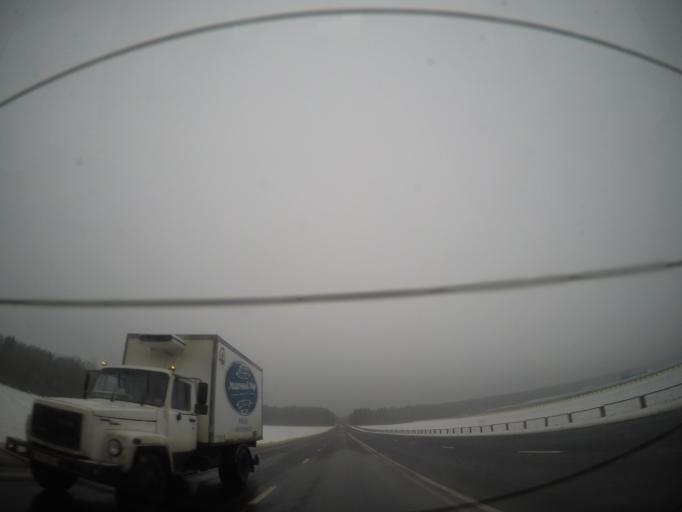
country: BY
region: Grodnenskaya
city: Hrodna
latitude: 53.6208
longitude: 23.8754
